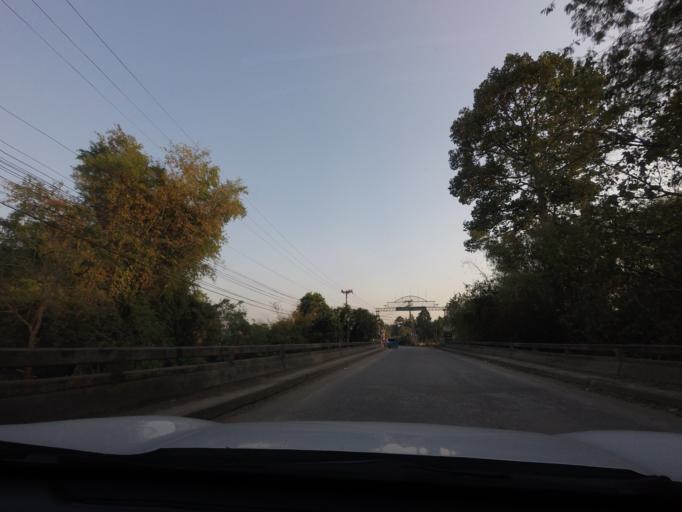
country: TH
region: Nakhon Ratchasima
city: Pak Chong
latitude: 14.6399
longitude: 101.4206
